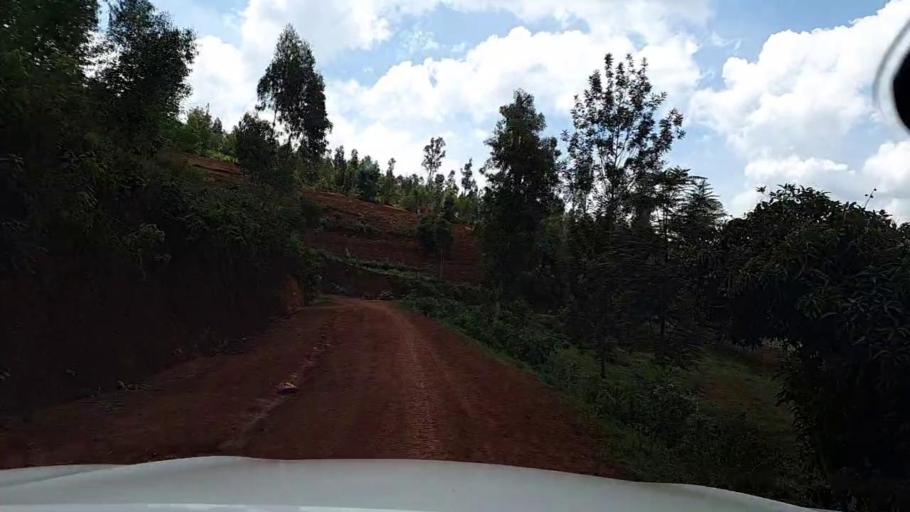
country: RW
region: Southern Province
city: Butare
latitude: -2.7439
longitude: 29.7666
